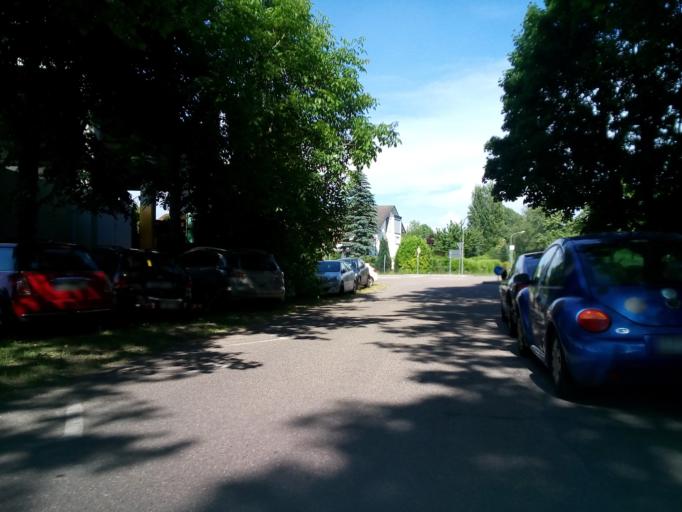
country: DE
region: Baden-Wuerttemberg
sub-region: Karlsruhe Region
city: Lichtenau
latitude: 48.7351
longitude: 7.9777
